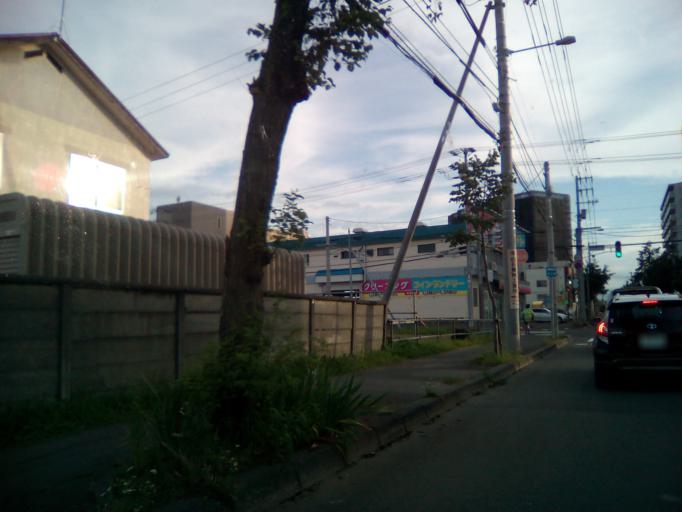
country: JP
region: Hokkaido
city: Sapporo
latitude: 43.0509
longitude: 141.3826
